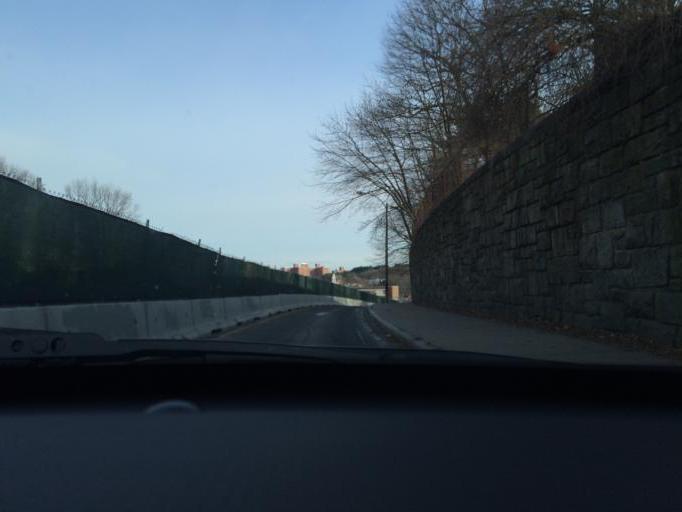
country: US
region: Massachusetts
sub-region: Suffolk County
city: Jamaica Plain
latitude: 42.3023
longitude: -71.1164
